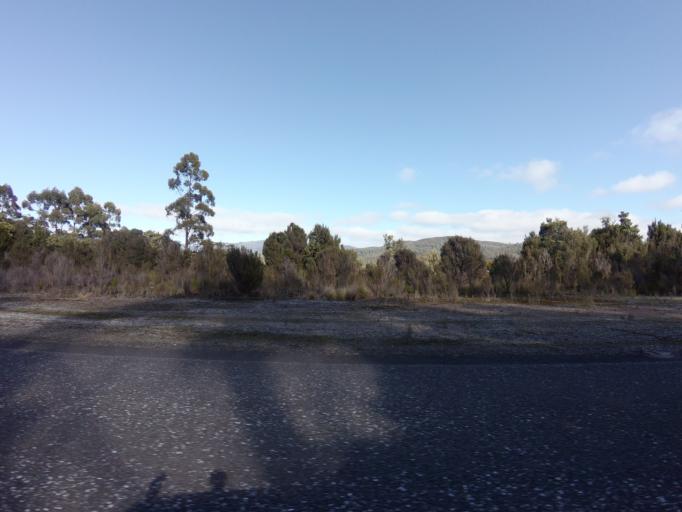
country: AU
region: Tasmania
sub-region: West Coast
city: Queenstown
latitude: -42.7766
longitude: 146.0573
